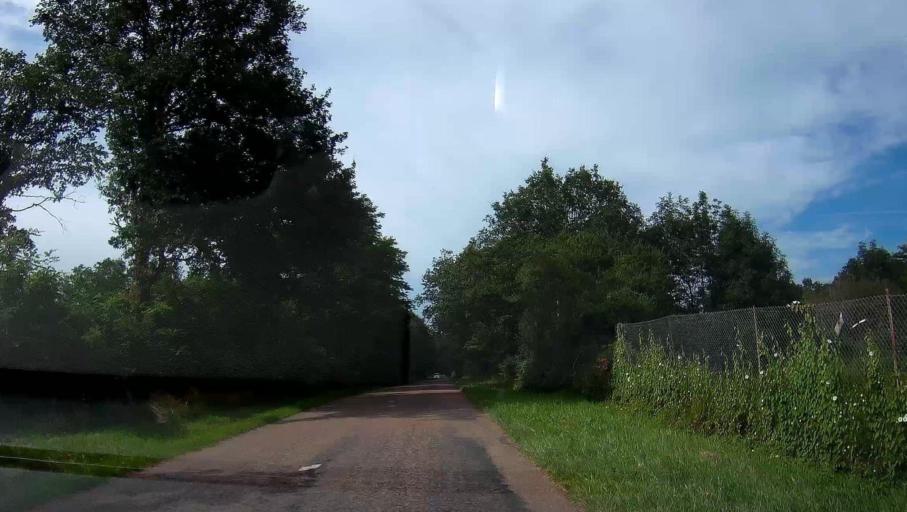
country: FR
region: Bourgogne
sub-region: Departement de Saone-et-Loire
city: Saint-Leger-sur-Dheune
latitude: 46.8732
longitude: 4.6329
